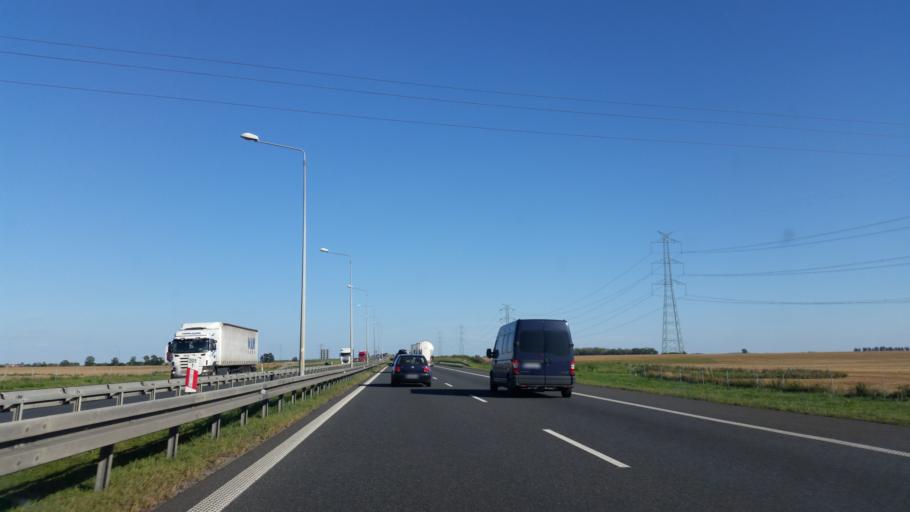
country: PL
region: Opole Voivodeship
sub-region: Powiat brzeski
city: Olszanka
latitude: 50.7538
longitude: 17.4359
